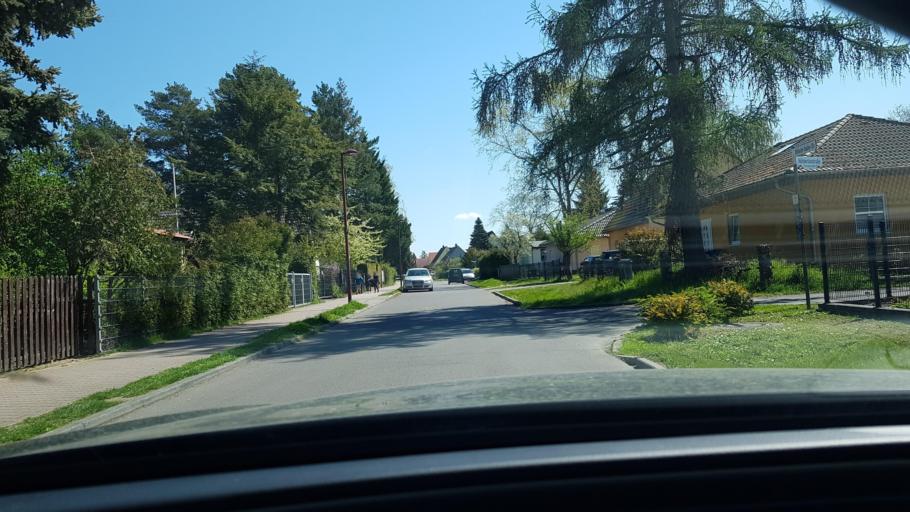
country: DE
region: Brandenburg
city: Rangsdorf
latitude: 52.3418
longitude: 13.4044
